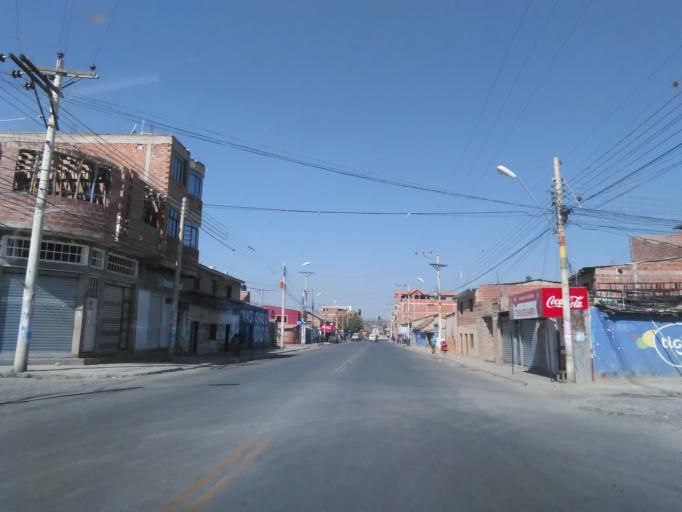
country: BO
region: Cochabamba
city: Sipe Sipe
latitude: -17.4047
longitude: -66.2816
